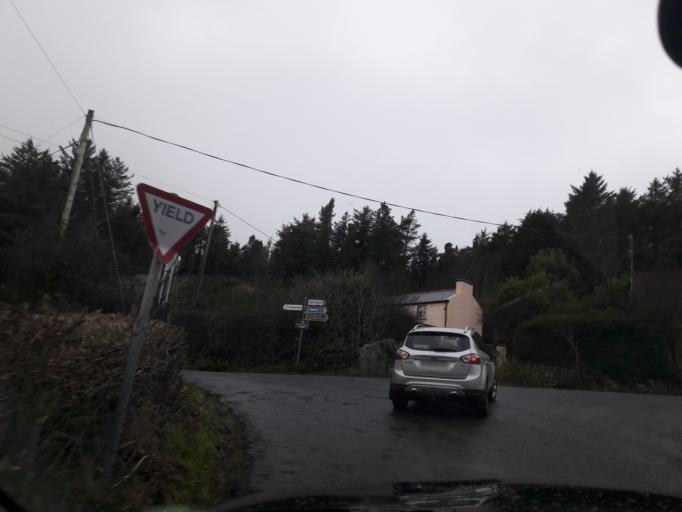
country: IE
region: Ulster
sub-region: County Donegal
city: Ramelton
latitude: 55.2510
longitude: -7.6371
